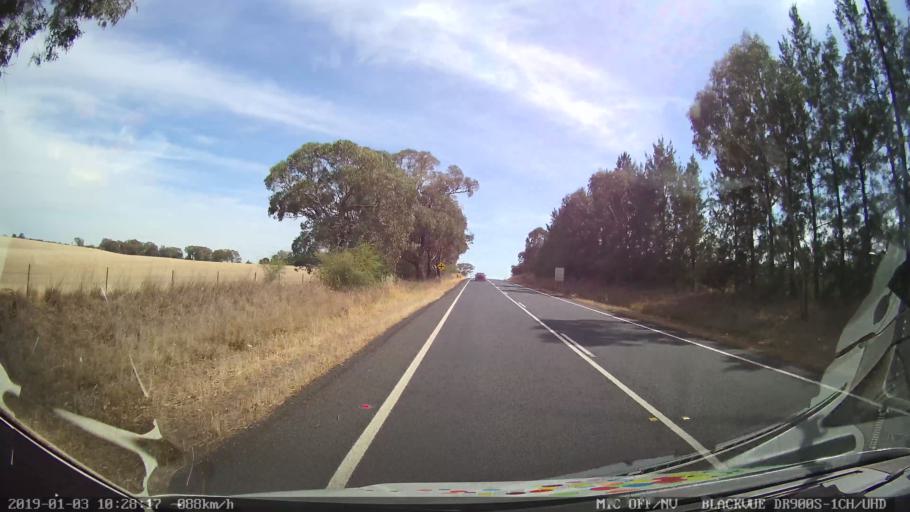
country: AU
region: New South Wales
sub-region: Young
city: Young
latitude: -34.3900
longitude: 148.2586
